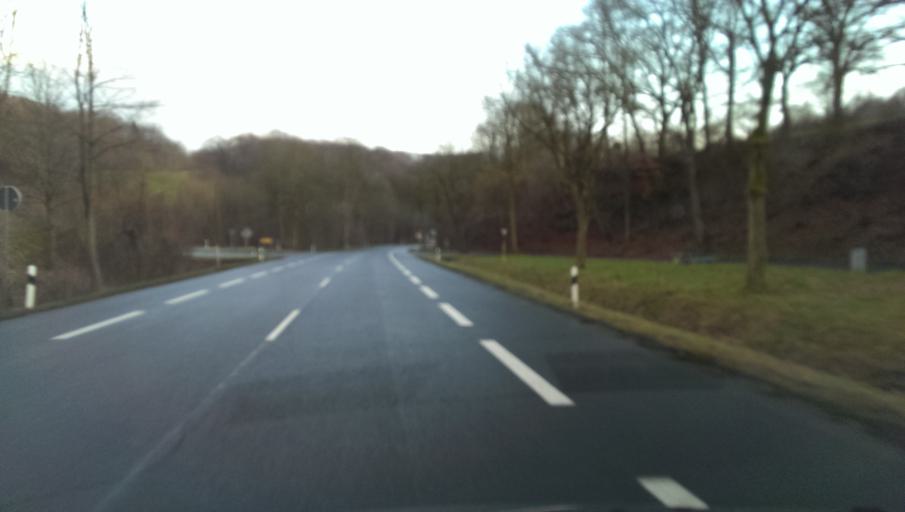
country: DE
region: Lower Saxony
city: Kreiensen
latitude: 51.8620
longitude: 9.9207
